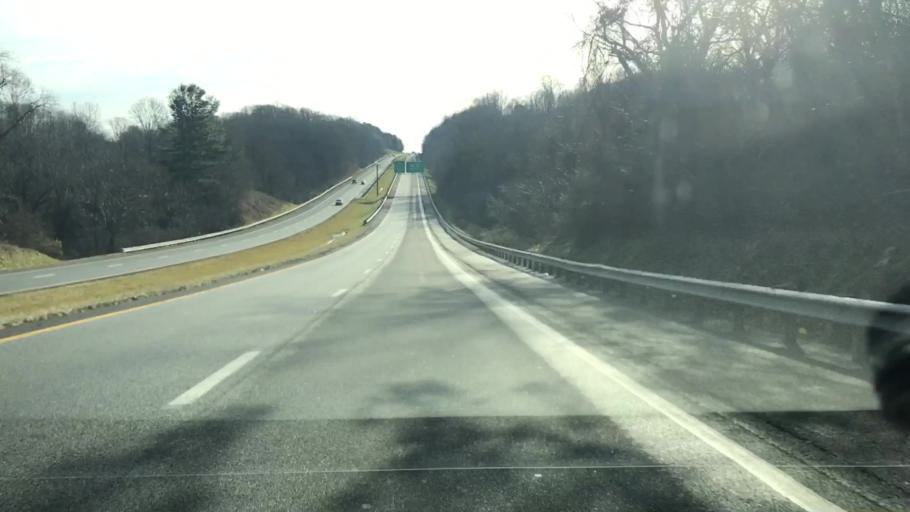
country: US
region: Virginia
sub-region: Montgomery County
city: Christiansburg
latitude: 37.1453
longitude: -80.3916
